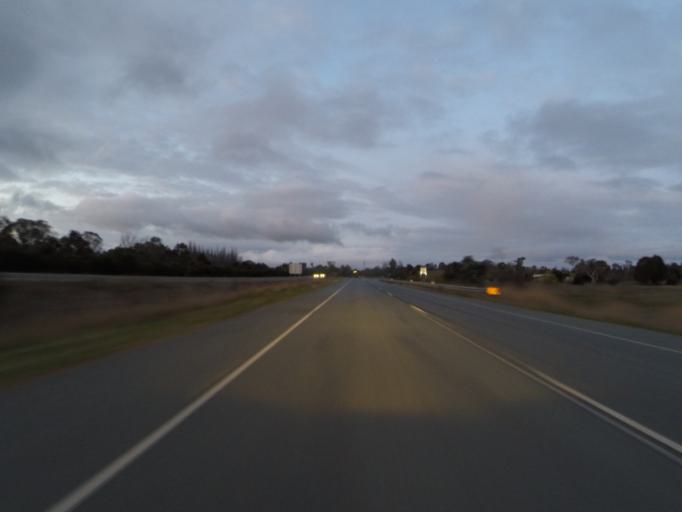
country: AU
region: Australian Capital Territory
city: Kaleen
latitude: -35.1972
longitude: 149.2181
